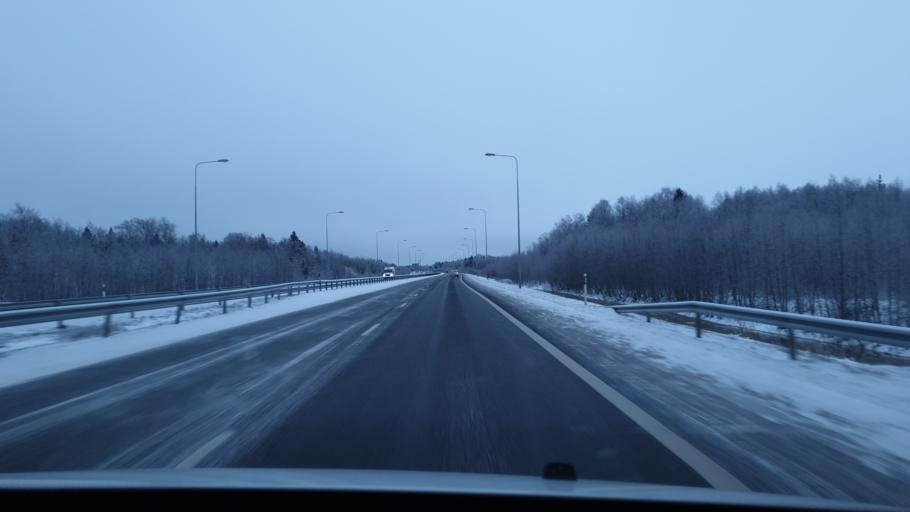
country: FI
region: Lapland
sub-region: Kemi-Tornio
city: Kemi
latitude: 65.7117
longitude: 24.6255
